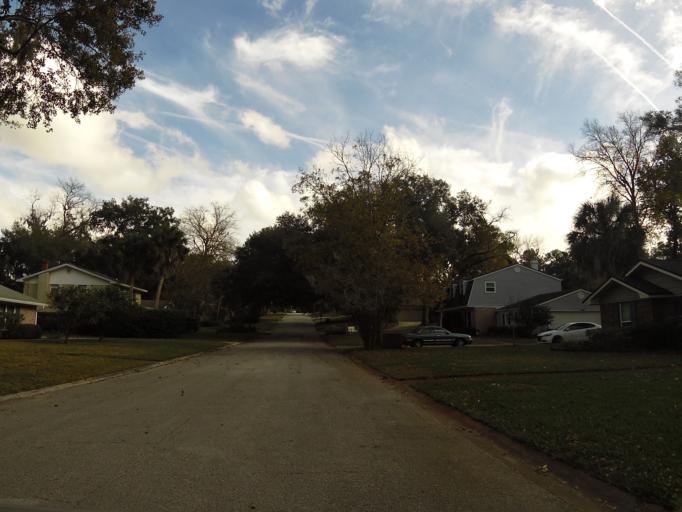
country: US
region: Florida
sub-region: Duval County
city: Atlantic Beach
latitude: 30.3766
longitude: -81.5155
